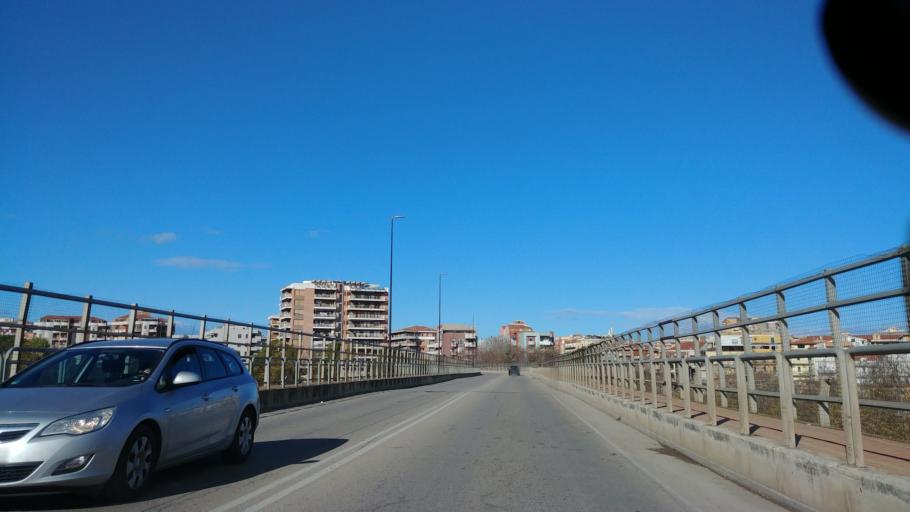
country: IT
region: Molise
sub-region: Provincia di Campobasso
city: Termoli
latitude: 41.9949
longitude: 14.9973
